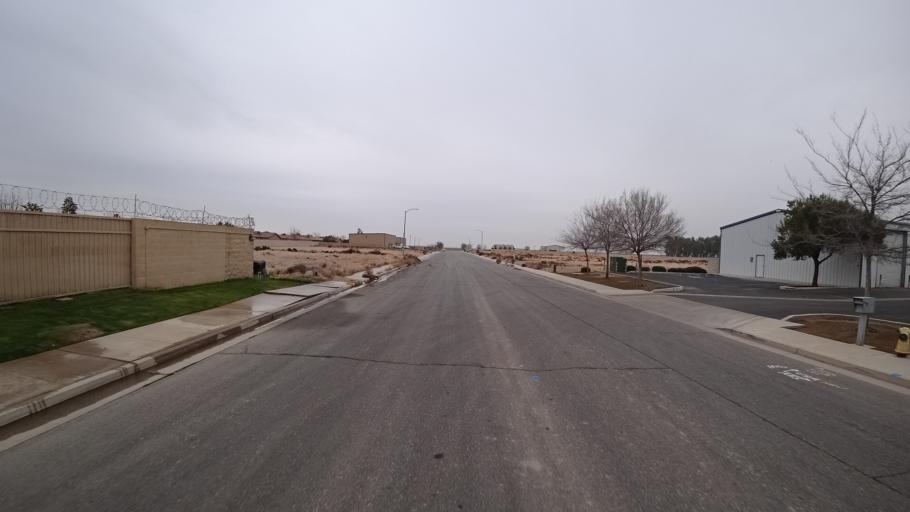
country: US
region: California
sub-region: Kern County
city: Bakersfield
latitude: 35.3498
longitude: -118.9531
